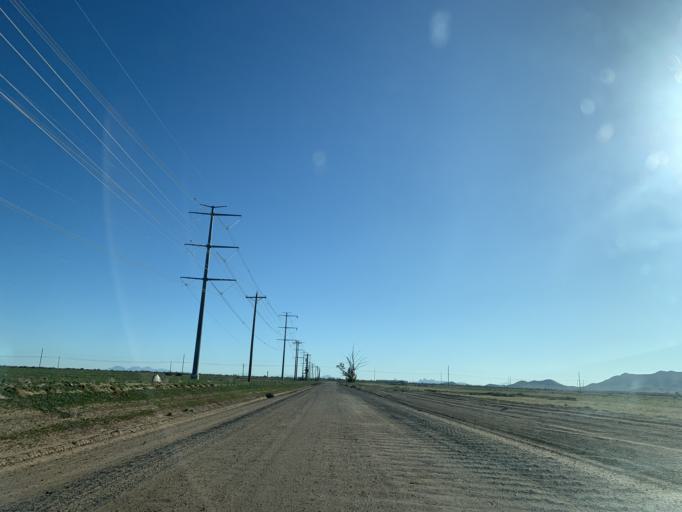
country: US
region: Arizona
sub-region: Pinal County
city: Casa Grande
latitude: 32.8540
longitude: -111.6710
